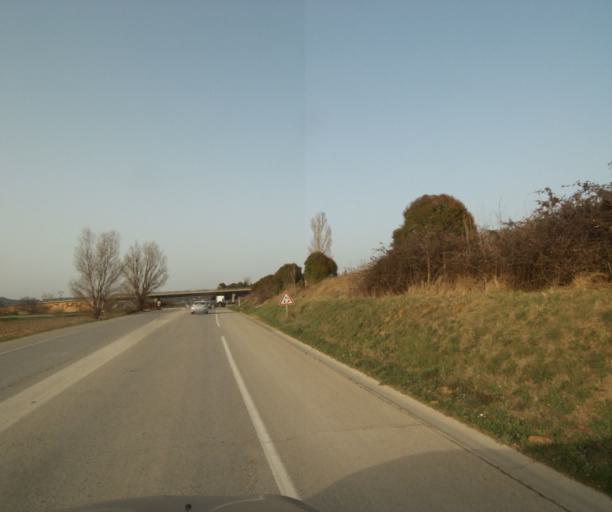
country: FR
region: Provence-Alpes-Cote d'Azur
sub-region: Departement des Bouches-du-Rhone
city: Eguilles
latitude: 43.5429
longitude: 5.3481
